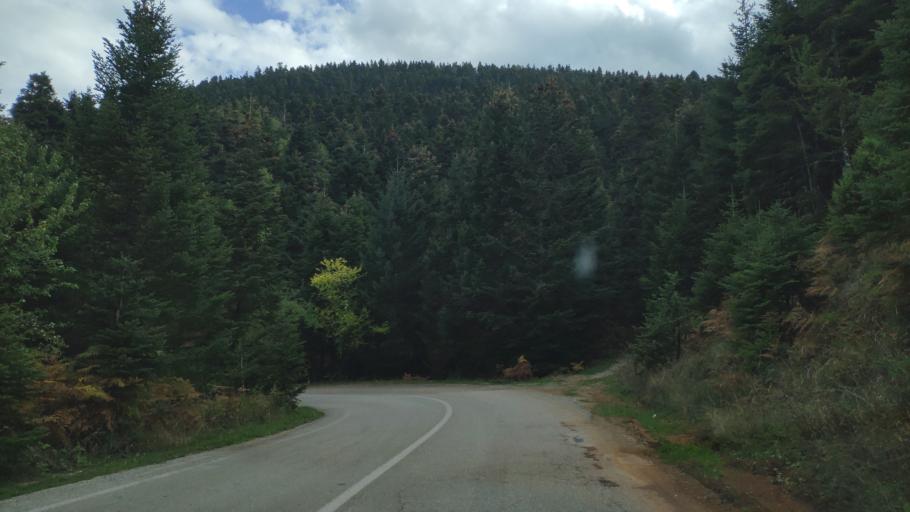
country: GR
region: Central Greece
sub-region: Nomos Fthiotidos
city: Stavros
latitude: 38.7302
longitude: 22.3542
